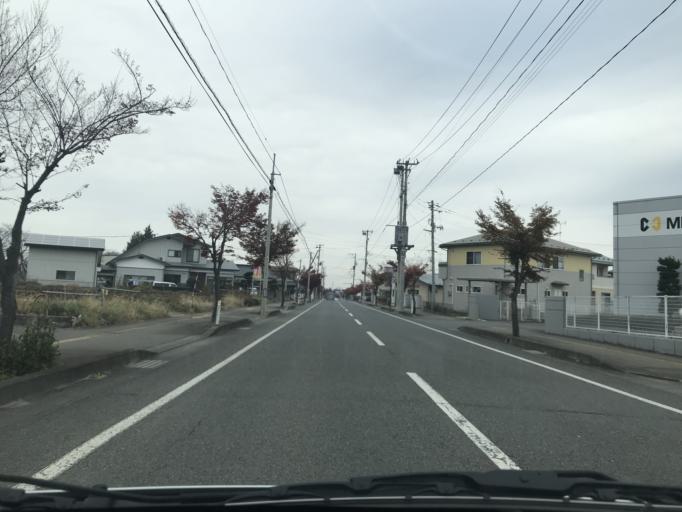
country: JP
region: Iwate
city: Mizusawa
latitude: 39.1202
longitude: 141.1235
